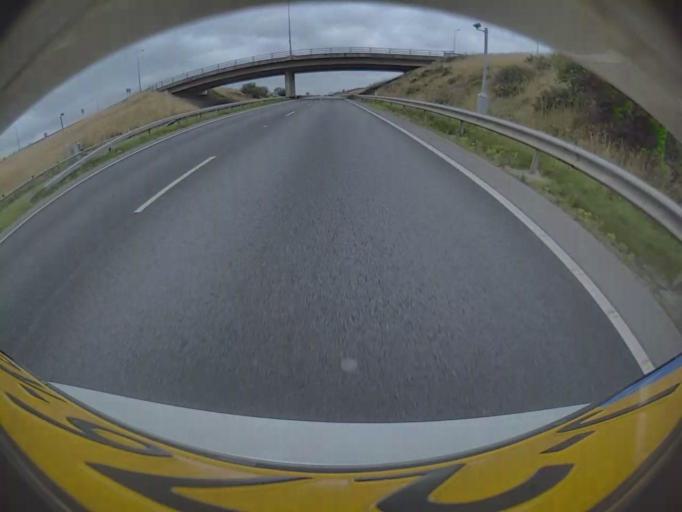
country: GB
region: Wales
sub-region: Anglesey
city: Gaerwen
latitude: 53.2260
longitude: -4.2599
